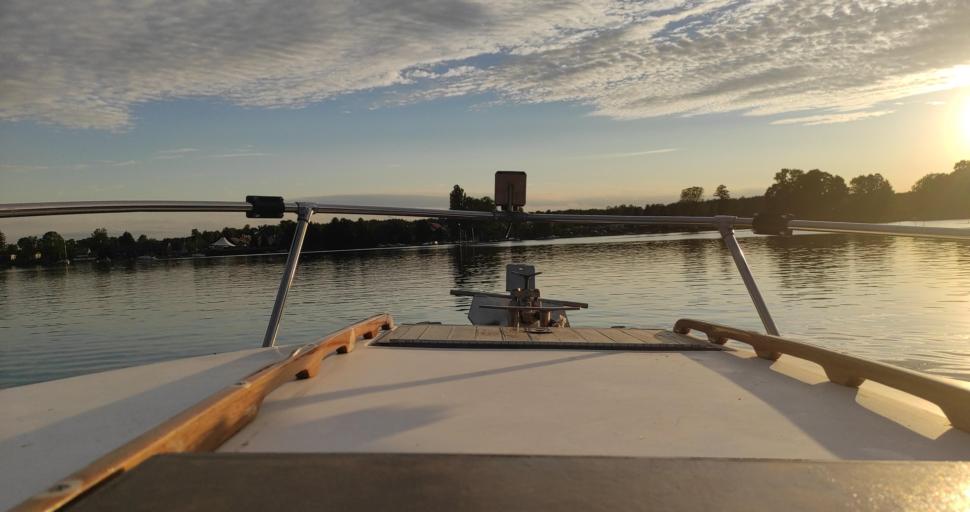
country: DE
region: Brandenburg
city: Friedland
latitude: 52.0229
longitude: 14.1816
